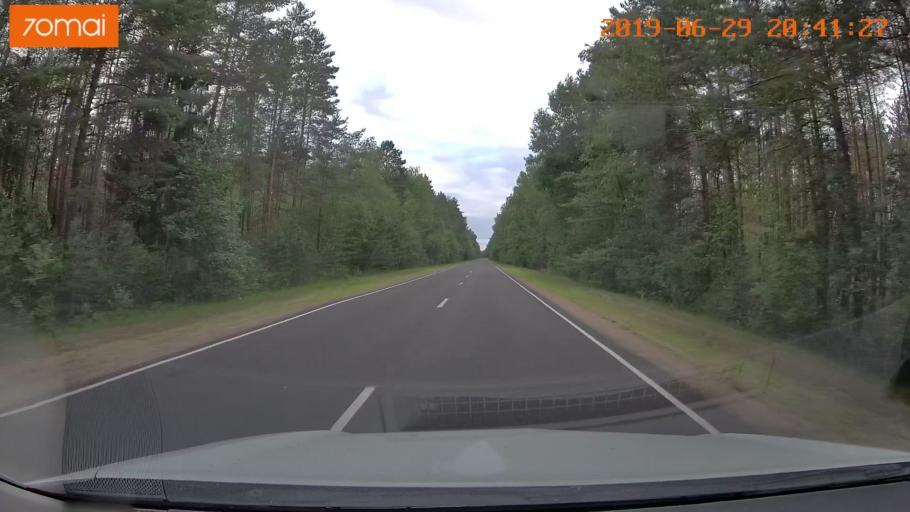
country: BY
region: Brest
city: Hantsavichy
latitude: 52.5858
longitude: 26.3394
